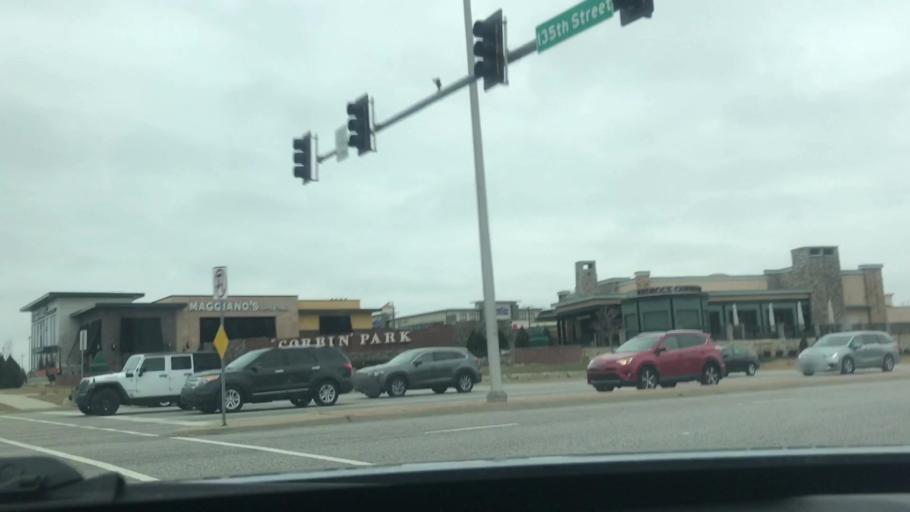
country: US
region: Kansas
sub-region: Johnson County
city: Lenexa
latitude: 38.8836
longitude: -94.6679
